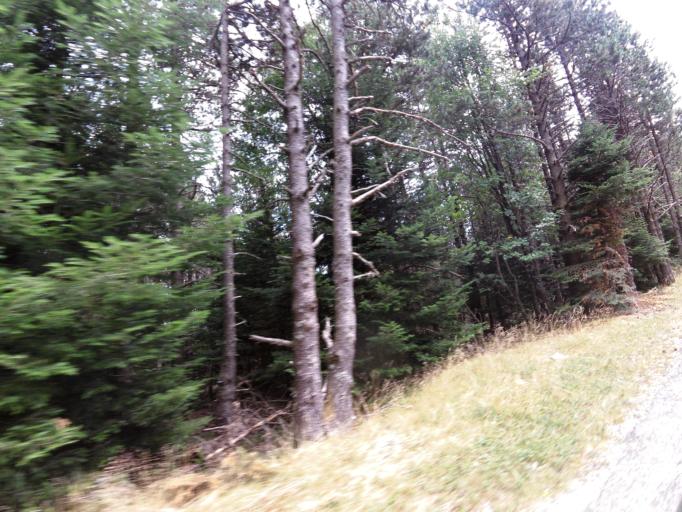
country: FR
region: Languedoc-Roussillon
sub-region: Departement du Gard
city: Valleraugue
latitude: 44.0614
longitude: 3.6049
